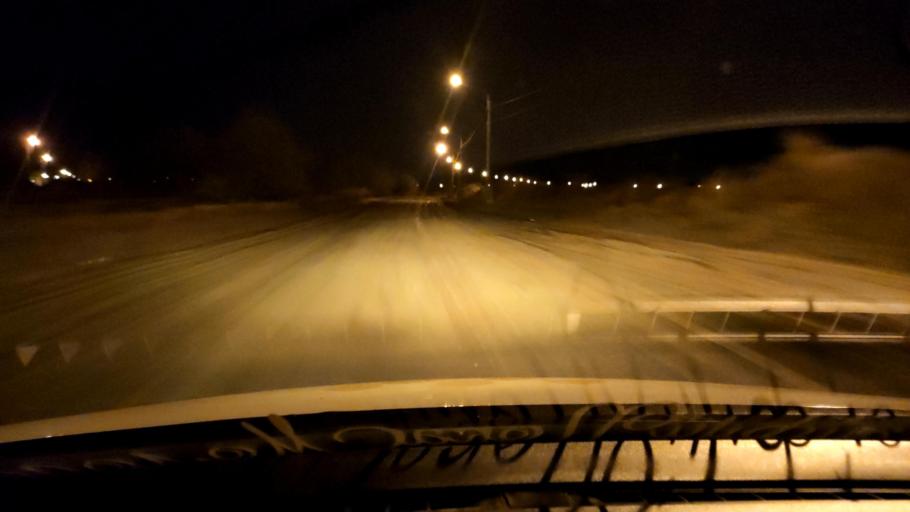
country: RU
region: Voronezj
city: Pridonskoy
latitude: 51.6962
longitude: 39.0684
